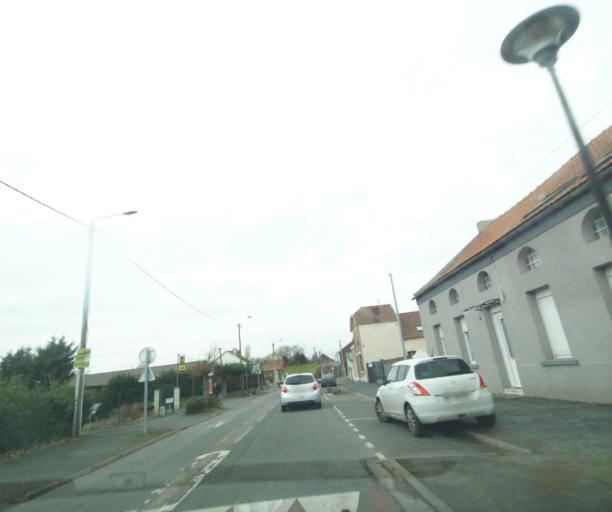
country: FR
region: Nord-Pas-de-Calais
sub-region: Departement du Nord
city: Vicq
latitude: 50.4117
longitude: 3.6006
